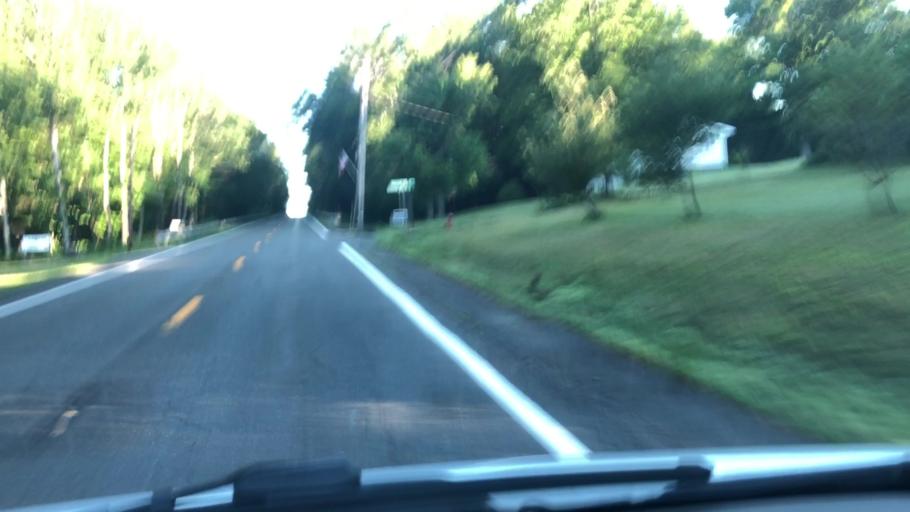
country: US
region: Massachusetts
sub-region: Hampshire County
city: Chesterfield
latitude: 42.3760
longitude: -72.9183
